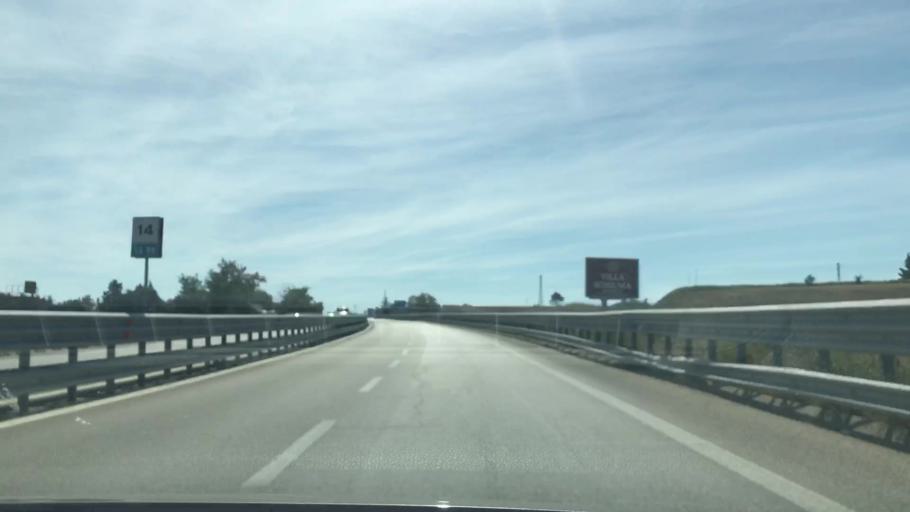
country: IT
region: Basilicate
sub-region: Provincia di Matera
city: Matera
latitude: 40.7089
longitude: 16.5812
